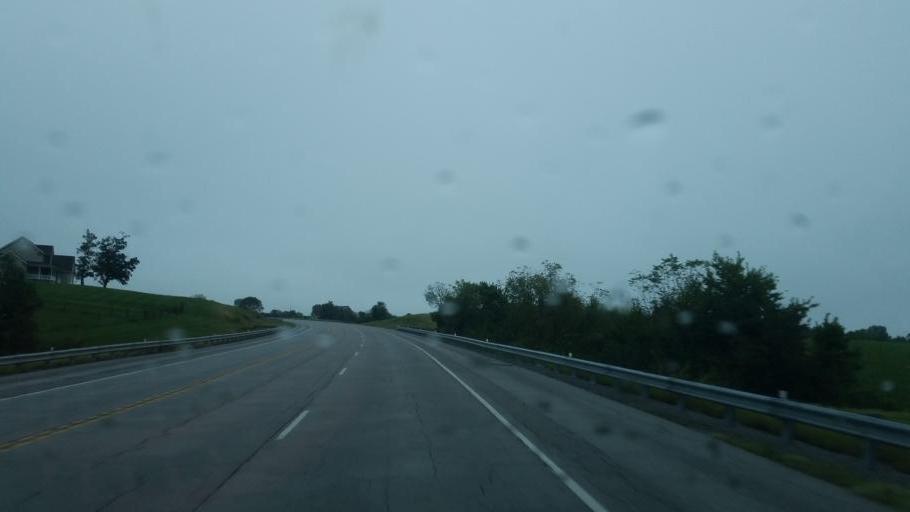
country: US
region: Kentucky
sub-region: Fleming County
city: Flemingsburg
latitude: 38.3969
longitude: -83.7175
